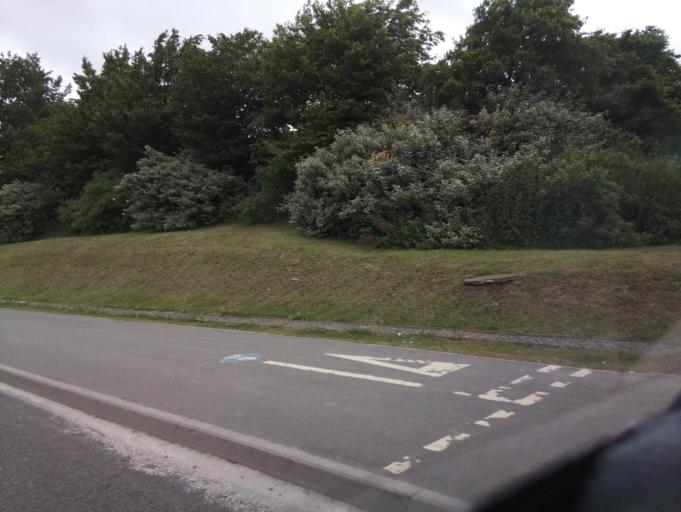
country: GB
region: England
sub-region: Leicestershire
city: Coalville
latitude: 52.7107
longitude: -1.3416
